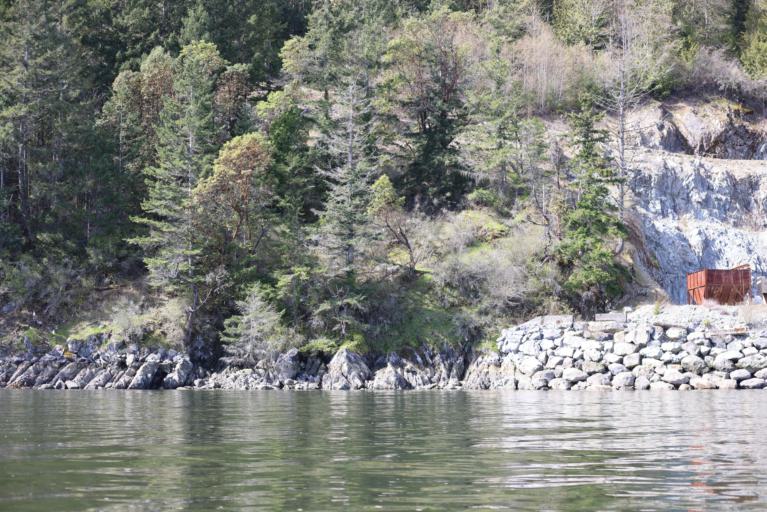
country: CA
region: British Columbia
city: North Saanich
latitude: 48.5817
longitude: -123.5200
